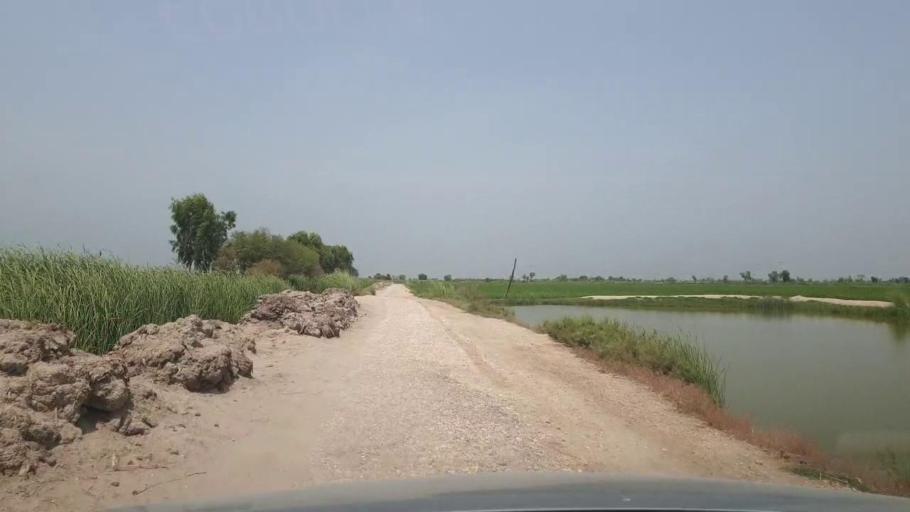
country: PK
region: Sindh
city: Garhi Yasin
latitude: 27.9258
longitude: 68.4334
